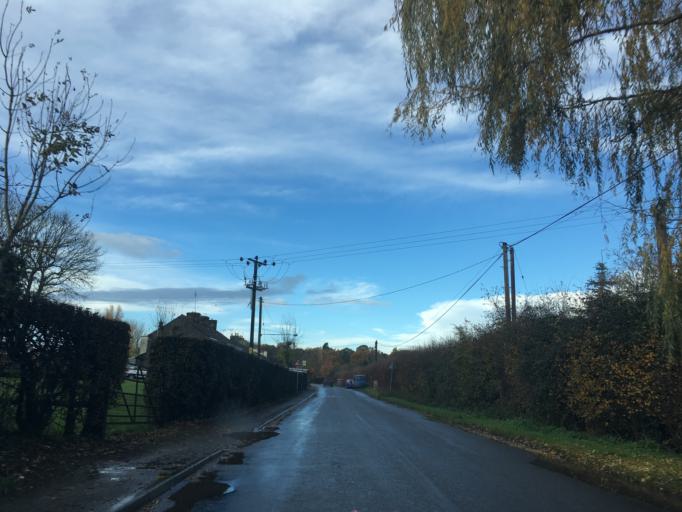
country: GB
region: England
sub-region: South Gloucestershire
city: Pucklechurch
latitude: 51.5099
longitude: -2.4623
